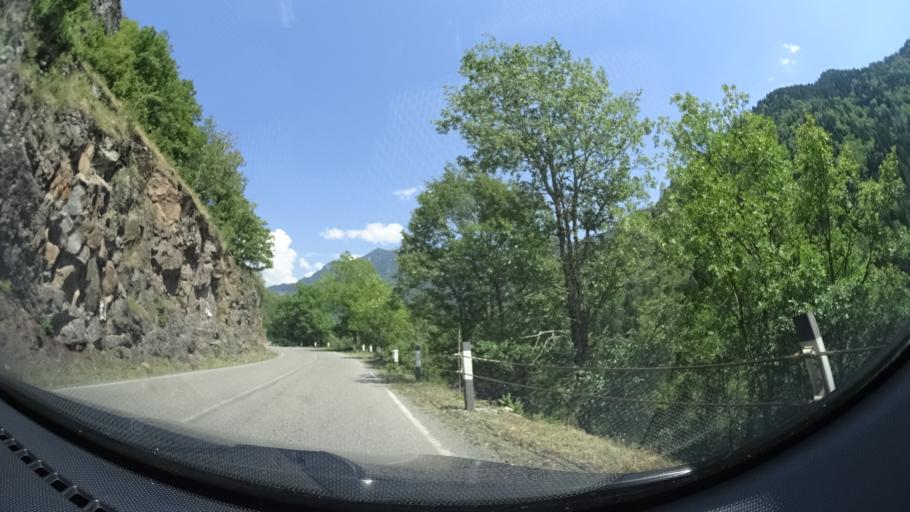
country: GE
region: Ajaria
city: Khulo
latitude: 41.6245
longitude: 42.2772
